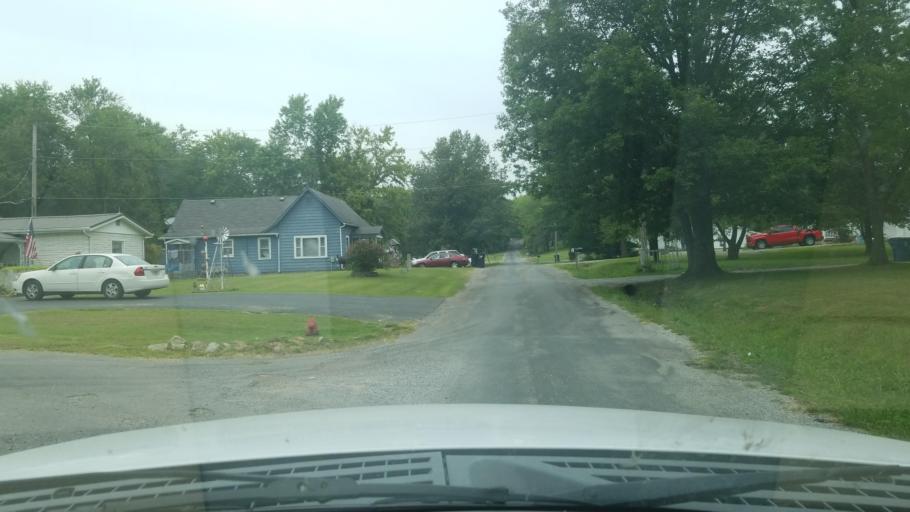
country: US
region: Illinois
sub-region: Saline County
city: Harrisburg
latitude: 37.8450
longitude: -88.6099
